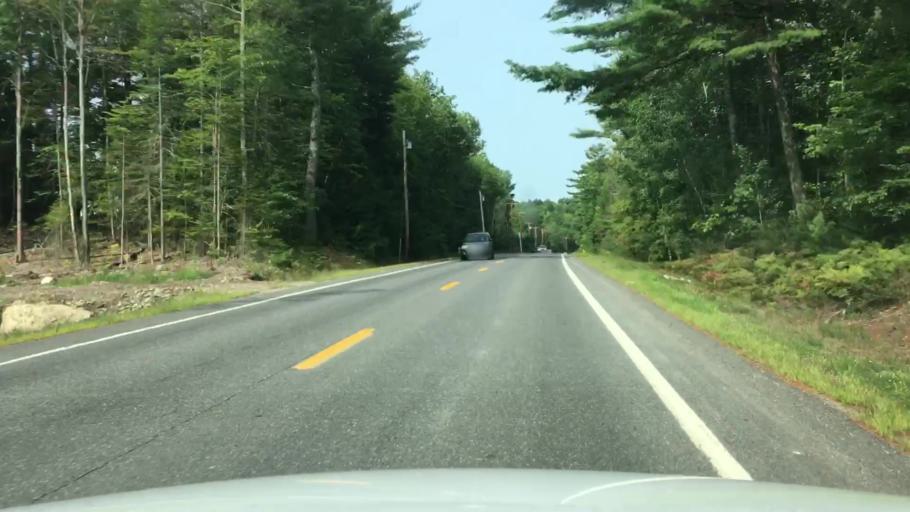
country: US
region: Maine
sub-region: Kennebec County
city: Chelsea
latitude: 44.3143
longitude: -69.7122
